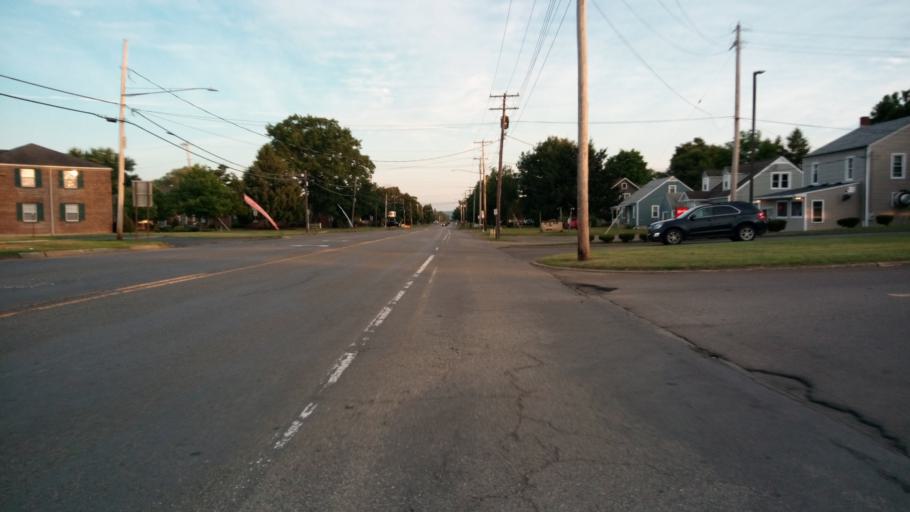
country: US
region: New York
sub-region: Chemung County
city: Horseheads
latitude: 42.1549
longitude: -76.8215
